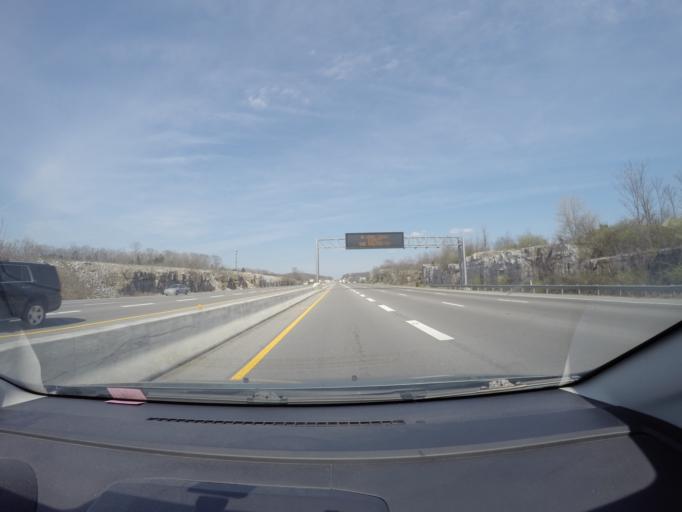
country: US
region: Tennessee
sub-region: Rutherford County
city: La Vergne
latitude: 36.0058
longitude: -86.6109
